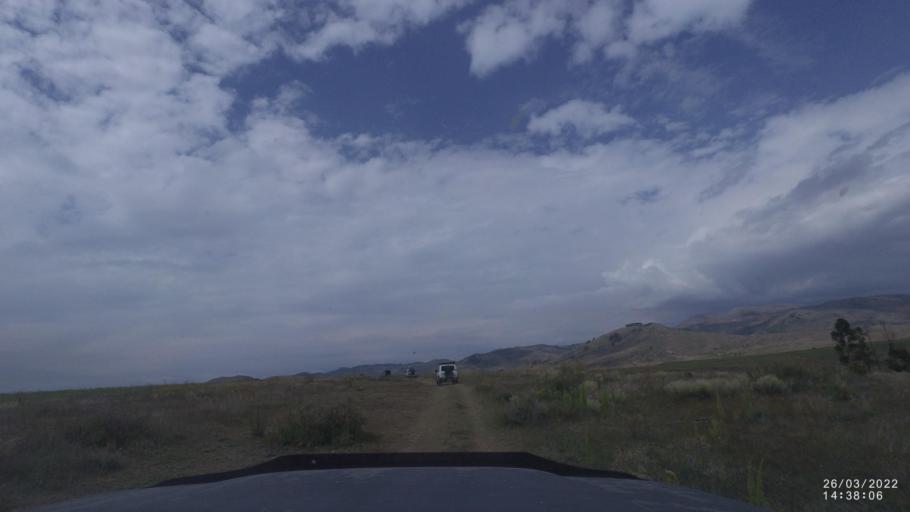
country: BO
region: Cochabamba
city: Cliza
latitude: -17.7380
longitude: -65.8628
